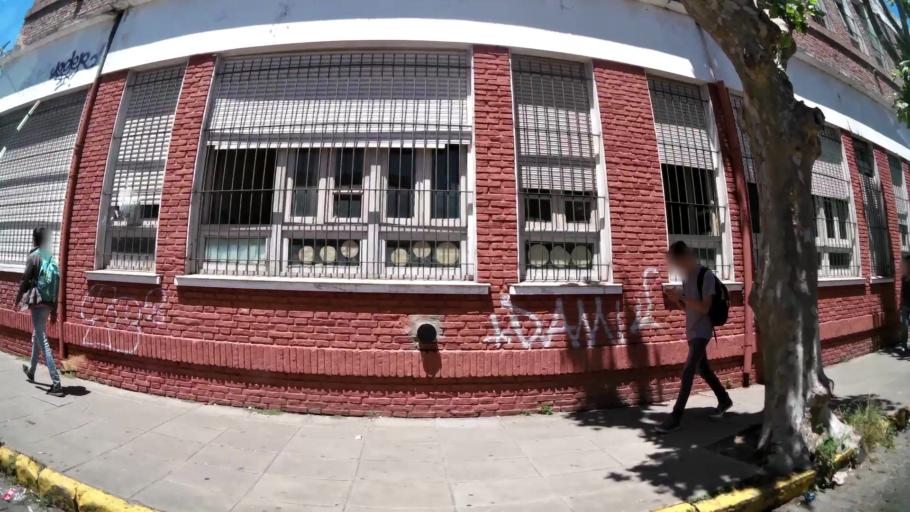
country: AR
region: Buenos Aires
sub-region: Partido de Tigre
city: Tigre
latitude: -34.4443
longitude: -58.5512
